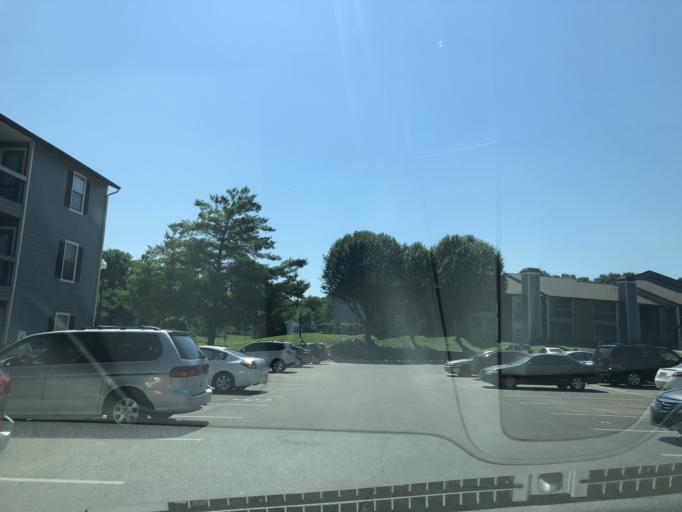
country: US
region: Tennessee
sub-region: Williamson County
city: Nolensville
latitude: 36.0427
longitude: -86.6684
